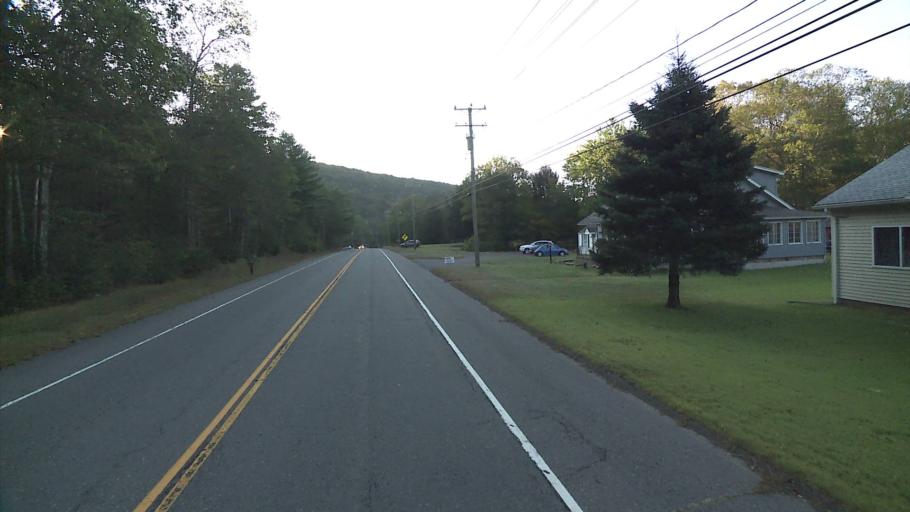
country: US
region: Connecticut
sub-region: Tolland County
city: Stafford Springs
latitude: 41.9230
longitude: -72.3021
